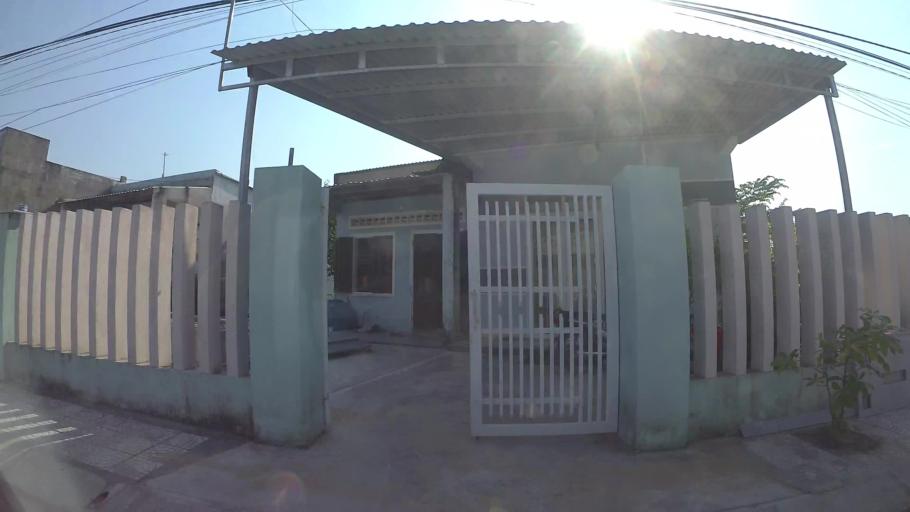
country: VN
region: Da Nang
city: Ngu Hanh Son
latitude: 15.9569
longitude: 108.2612
